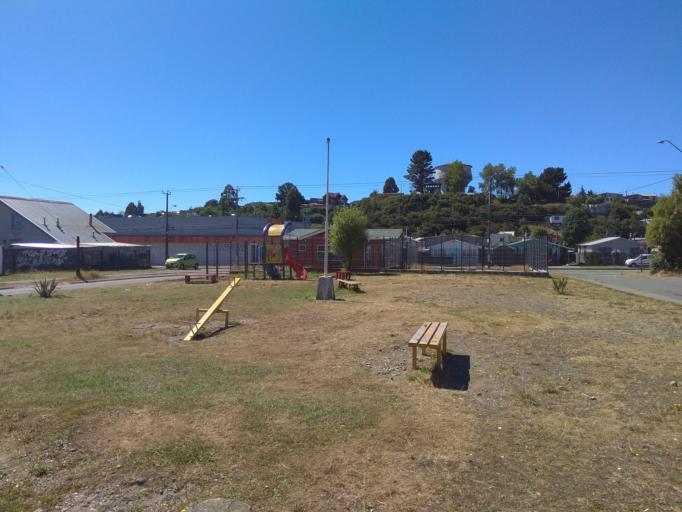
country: CL
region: Los Lagos
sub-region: Provincia de Llanquihue
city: Puerto Montt
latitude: -41.4612
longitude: -72.9376
